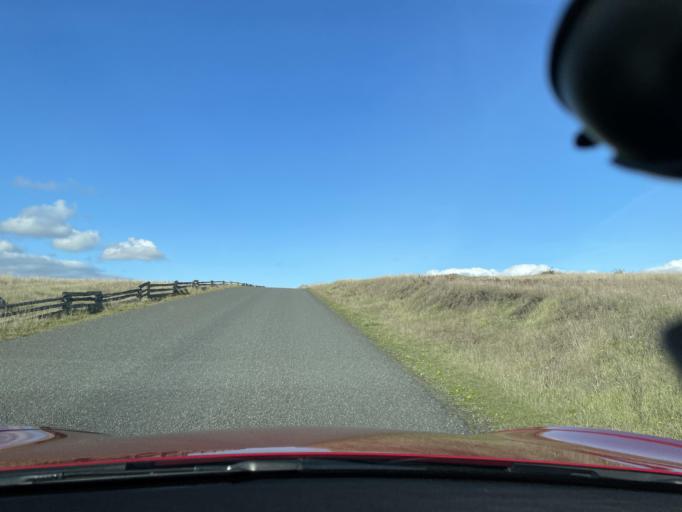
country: US
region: Washington
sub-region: San Juan County
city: Friday Harbor
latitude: 48.4577
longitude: -123.0015
